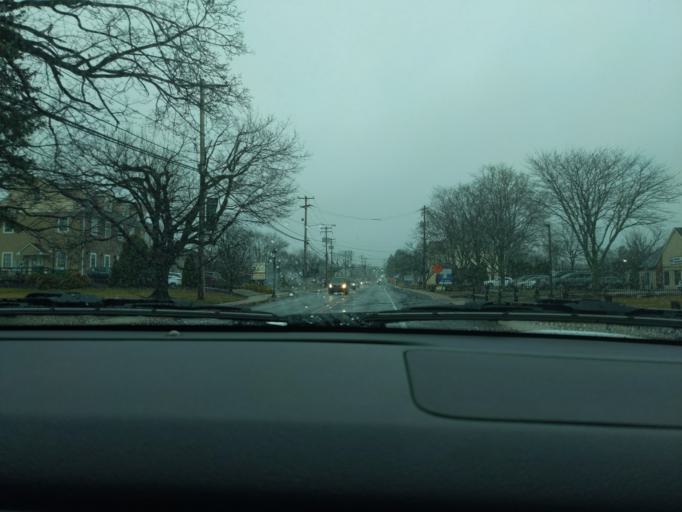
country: US
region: Pennsylvania
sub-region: Bucks County
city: Dublin
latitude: 40.3758
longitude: -75.2097
